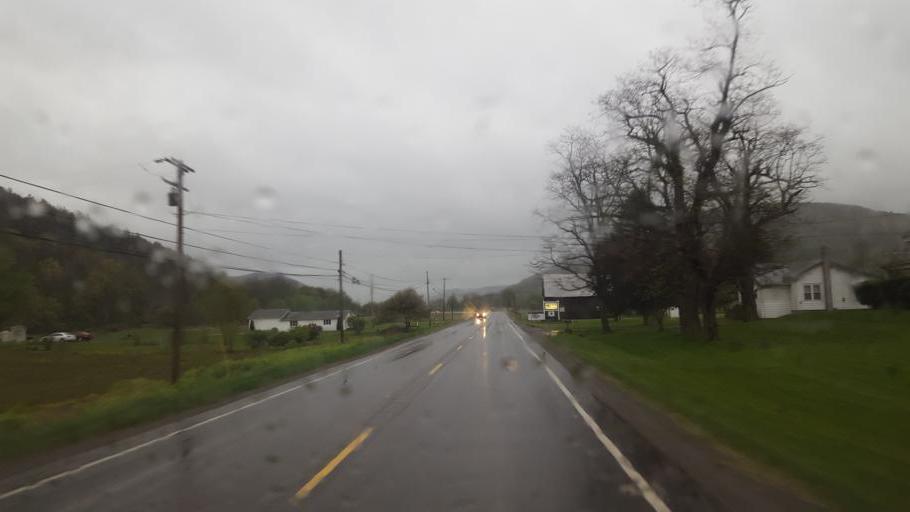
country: US
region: Pennsylvania
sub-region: Tioga County
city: Westfield
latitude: 41.9133
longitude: -77.5867
